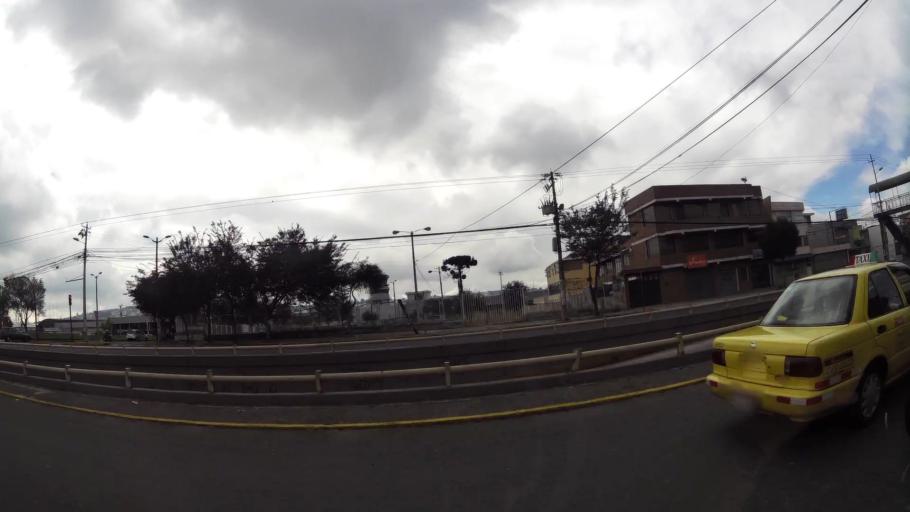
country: EC
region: Pichincha
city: Quito
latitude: -0.1466
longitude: -78.4913
